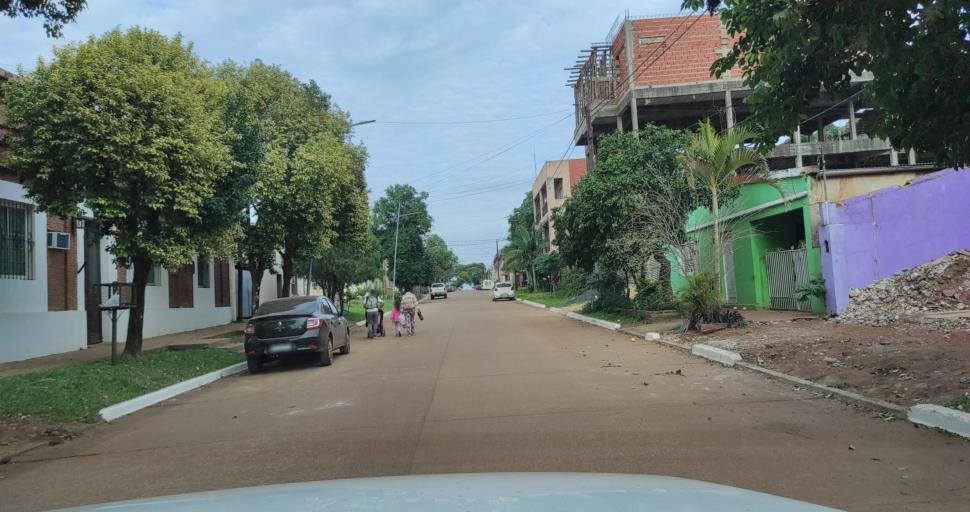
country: AR
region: Corrientes
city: Santo Tome
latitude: -28.5481
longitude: -56.0348
